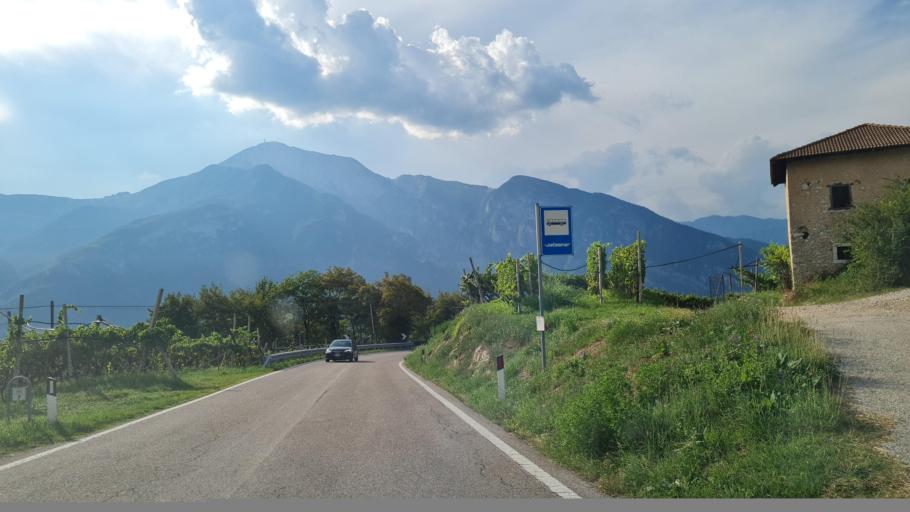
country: IT
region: Trentino-Alto Adige
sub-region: Provincia di Trento
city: Mattarello
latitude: 46.0123
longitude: 11.1477
